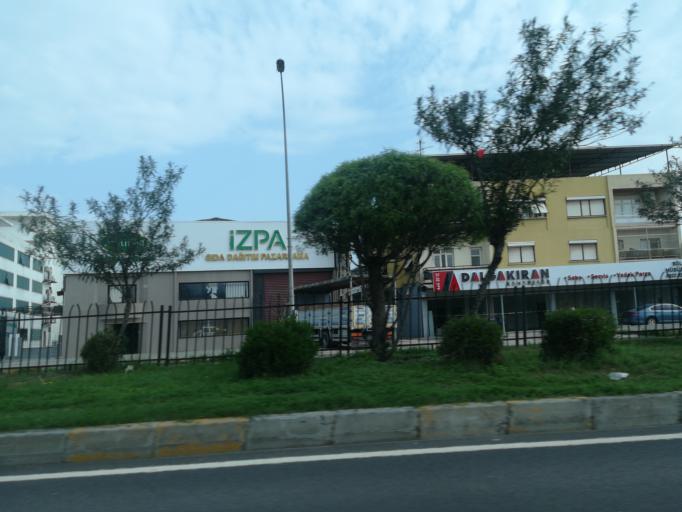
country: TR
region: Adana
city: Yuregir
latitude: 36.9862
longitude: 35.3602
